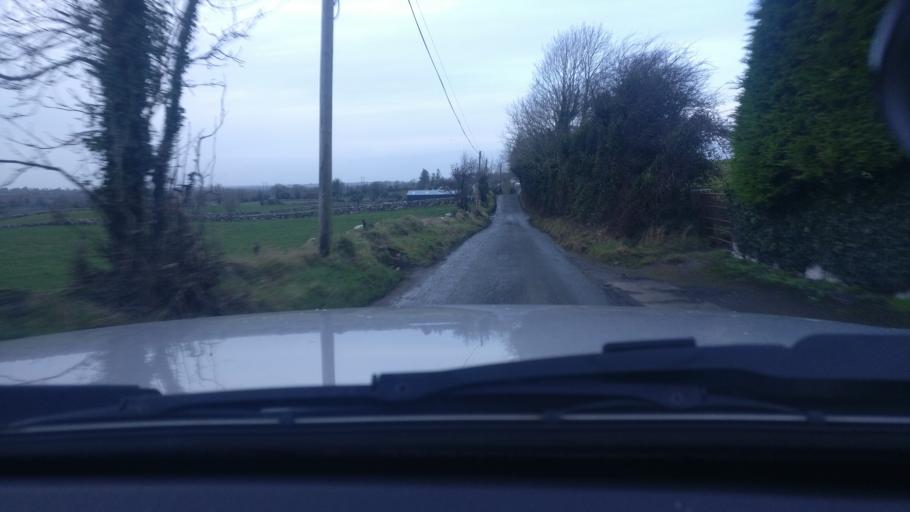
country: IE
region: Connaught
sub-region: County Galway
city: Loughrea
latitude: 53.1770
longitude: -8.5891
